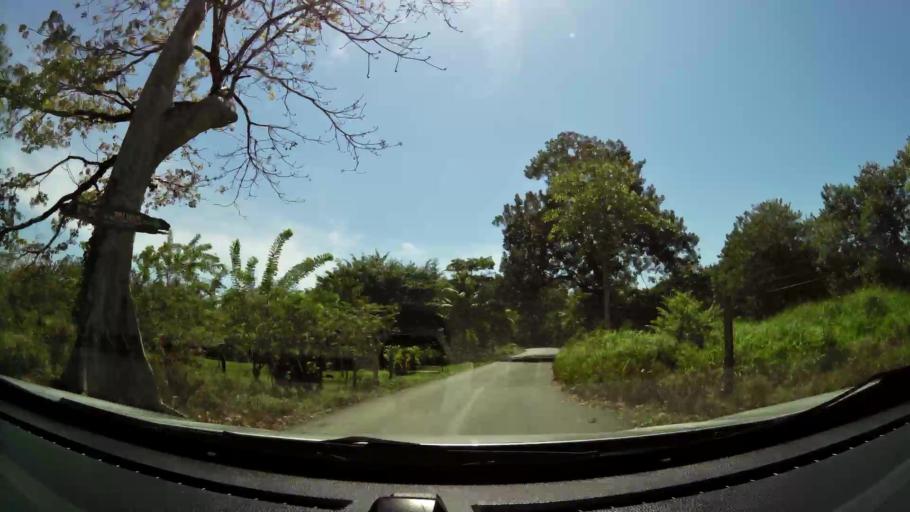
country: CR
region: Puntarenas
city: Quepos
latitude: 9.3214
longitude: -83.9581
